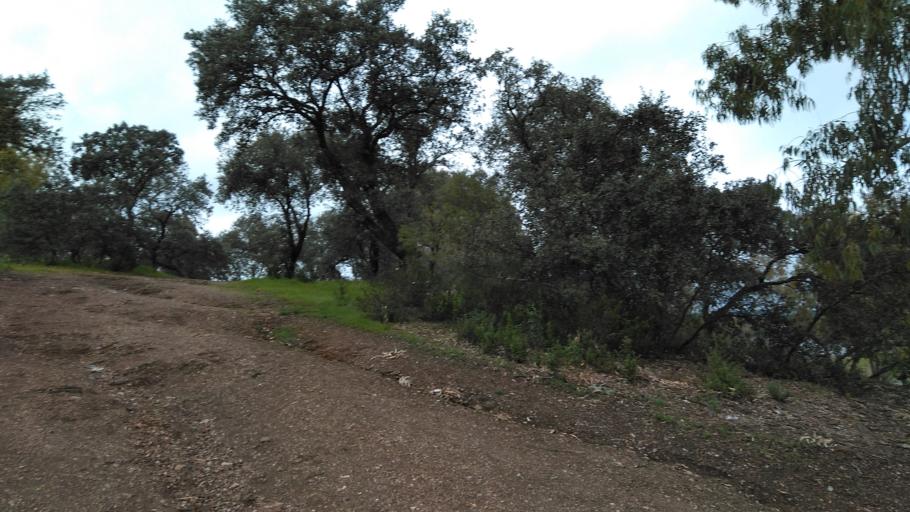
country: ES
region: Andalusia
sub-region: Provincia de Sevilla
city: El Ronquillo
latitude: 37.7102
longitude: -6.1126
